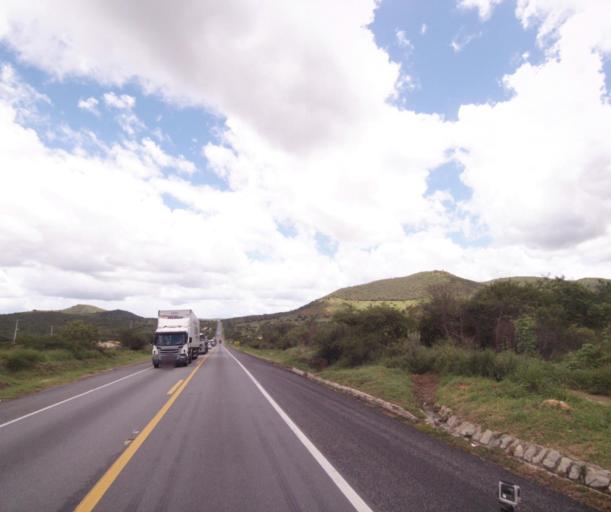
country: BR
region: Bahia
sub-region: Pocoes
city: Pocoes
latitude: -14.3549
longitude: -40.3363
